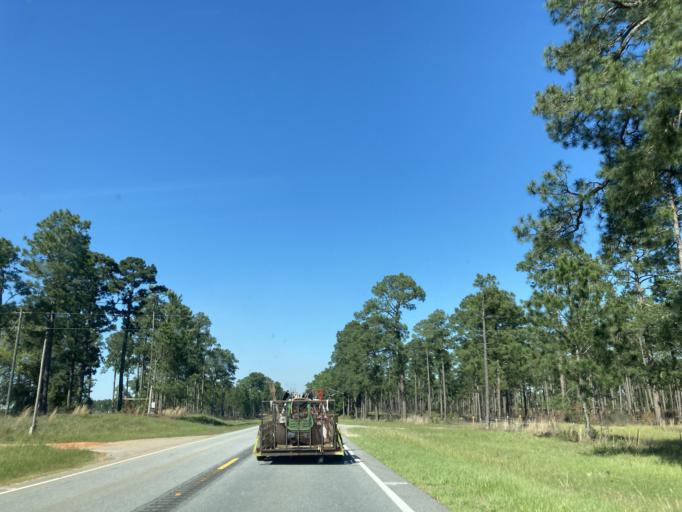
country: US
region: Georgia
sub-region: Baker County
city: Newton
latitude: 31.3622
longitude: -84.2932
